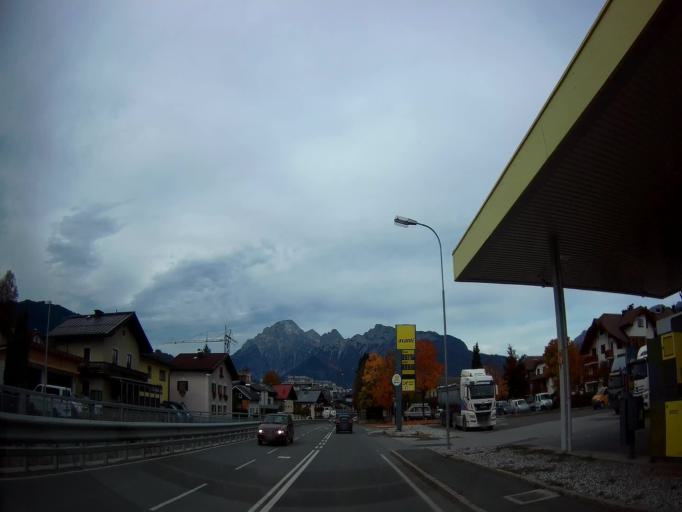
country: AT
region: Salzburg
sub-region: Politischer Bezirk Zell am See
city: Saalfelden am Steinernen Meer
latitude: 47.4231
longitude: 12.8499
